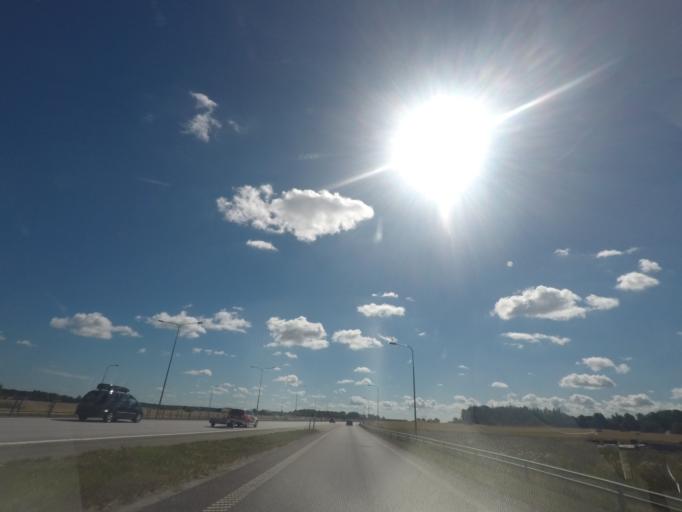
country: SE
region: Uppsala
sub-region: Uppsala Kommun
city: Gamla Uppsala
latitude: 59.8860
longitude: 17.6749
